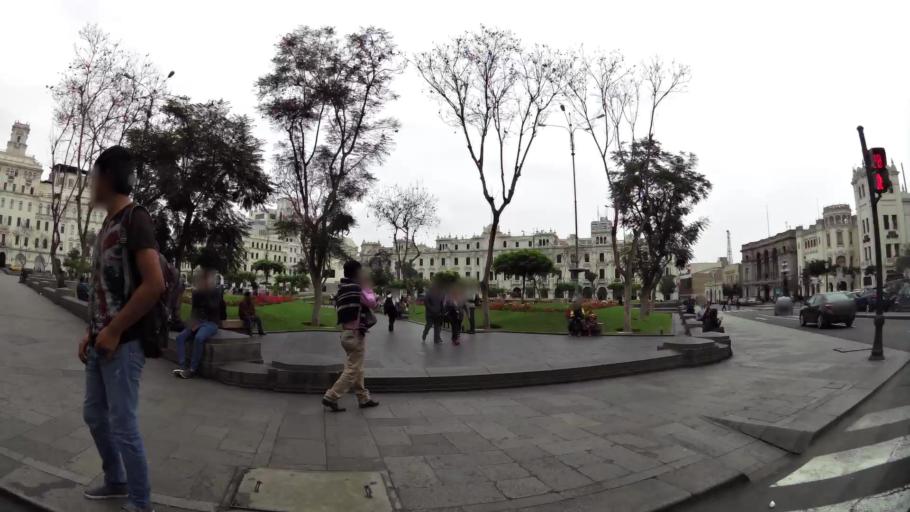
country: PE
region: Lima
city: Lima
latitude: -12.0511
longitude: -77.0347
